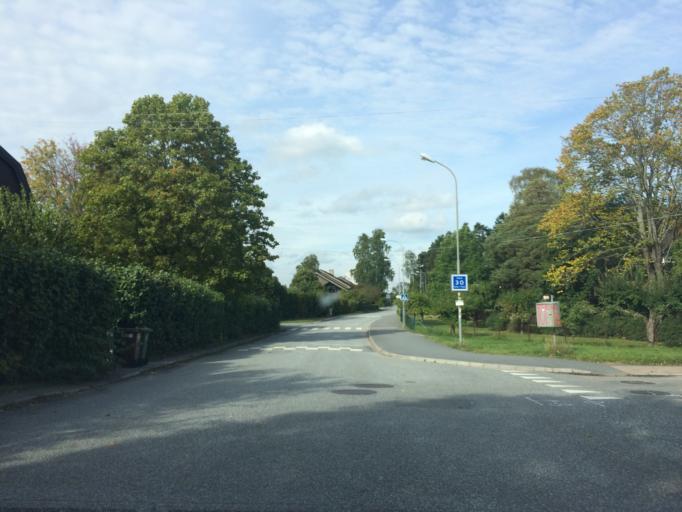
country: SE
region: Stockholm
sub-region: Sollentuna Kommun
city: Sollentuna
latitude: 59.4369
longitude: 17.9485
